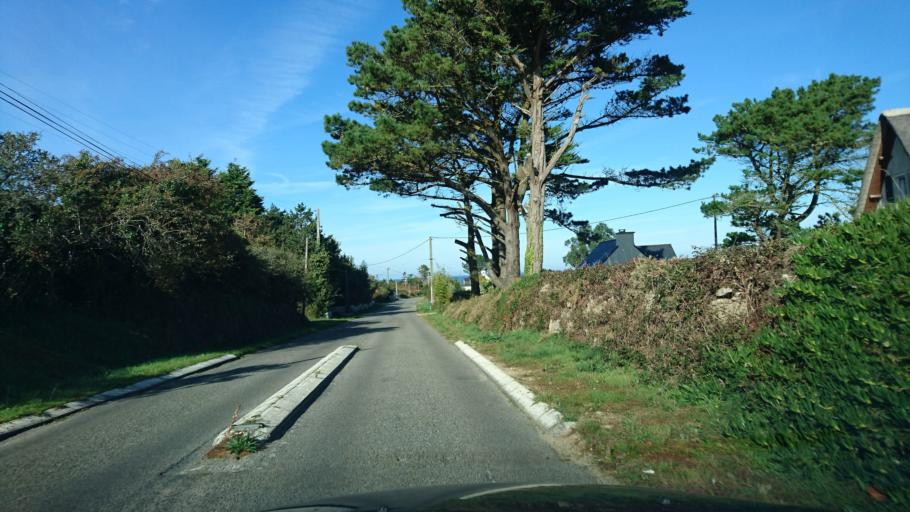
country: FR
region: Brittany
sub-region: Departement du Finistere
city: Lampaul-Plouarzel
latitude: 48.4323
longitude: -4.7692
